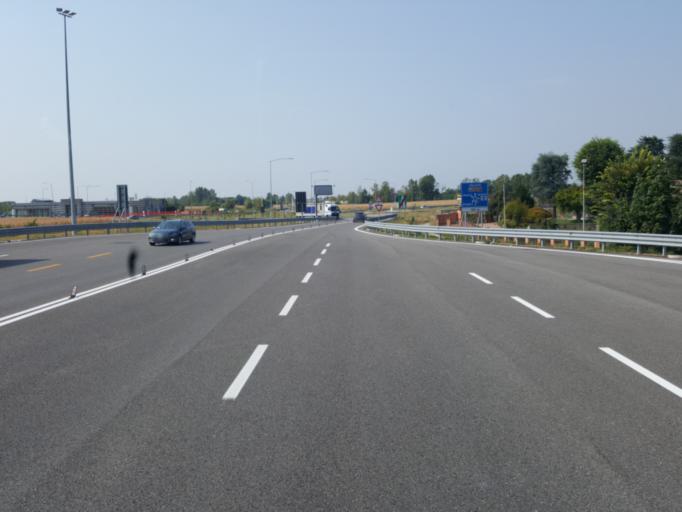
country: IT
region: Lombardy
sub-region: Provincia di Bergamo
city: Caravaggio
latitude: 45.5061
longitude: 9.6275
